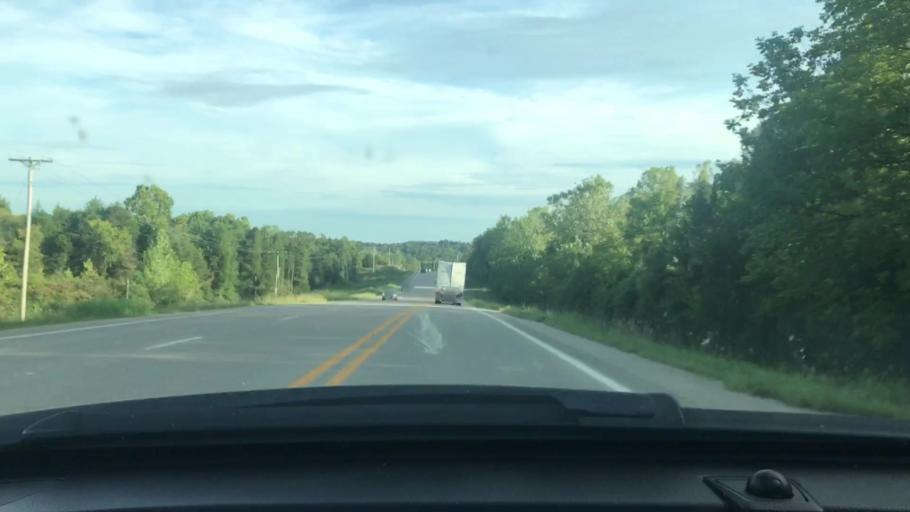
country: US
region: Arkansas
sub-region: Lawrence County
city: Hoxie
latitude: 36.1477
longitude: -91.1599
